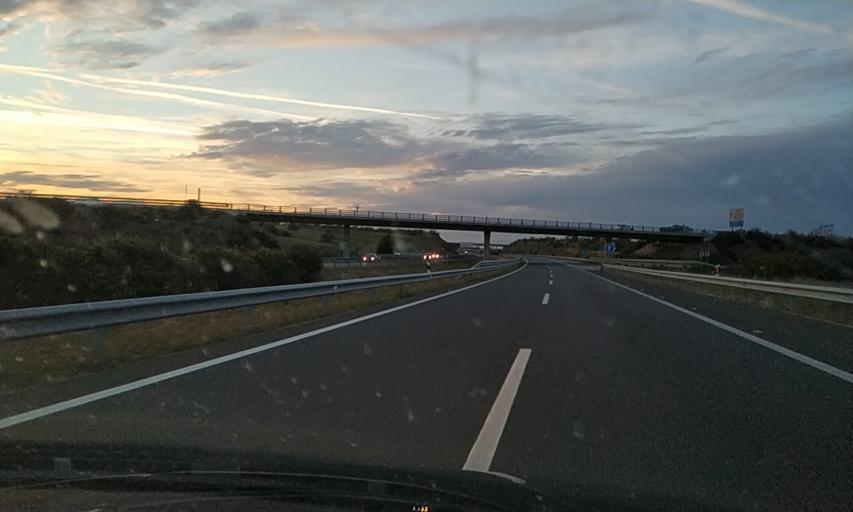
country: ES
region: Extremadura
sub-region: Provincia de Caceres
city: Caceres
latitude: 39.4309
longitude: -6.4051
